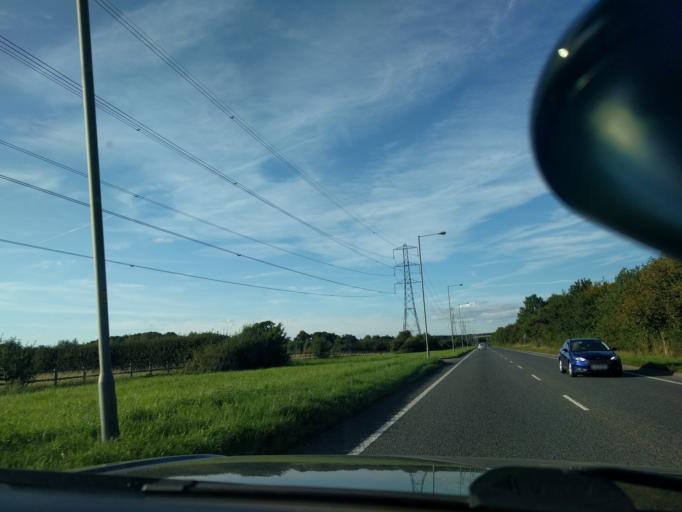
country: GB
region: England
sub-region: Wiltshire
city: Chippenham
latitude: 51.4560
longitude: -2.1515
